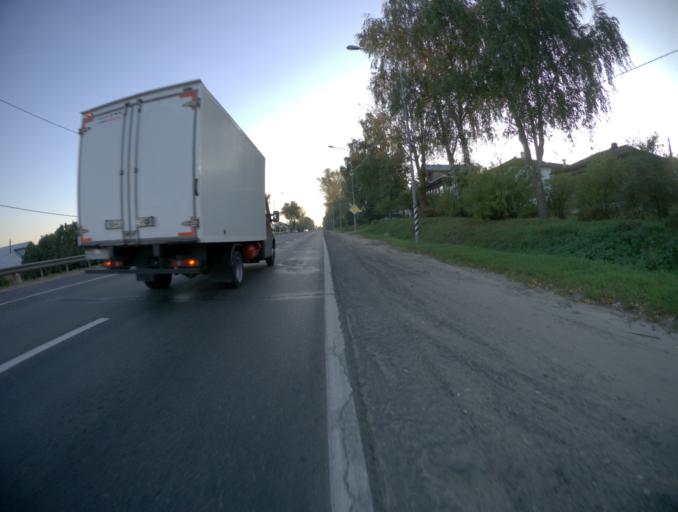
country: RU
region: Vladimir
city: Bogolyubovo
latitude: 56.1928
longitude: 40.5288
